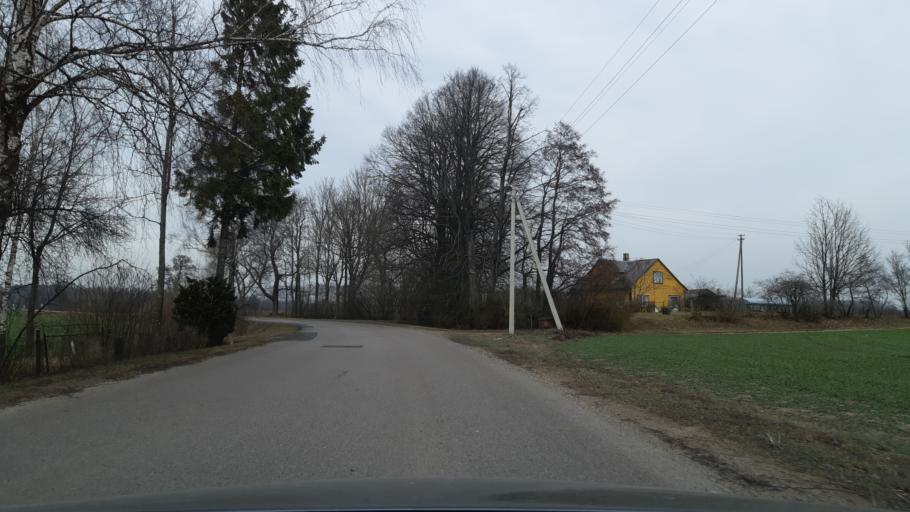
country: LT
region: Marijampoles apskritis
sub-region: Marijampole Municipality
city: Marijampole
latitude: 54.7227
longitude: 23.3366
